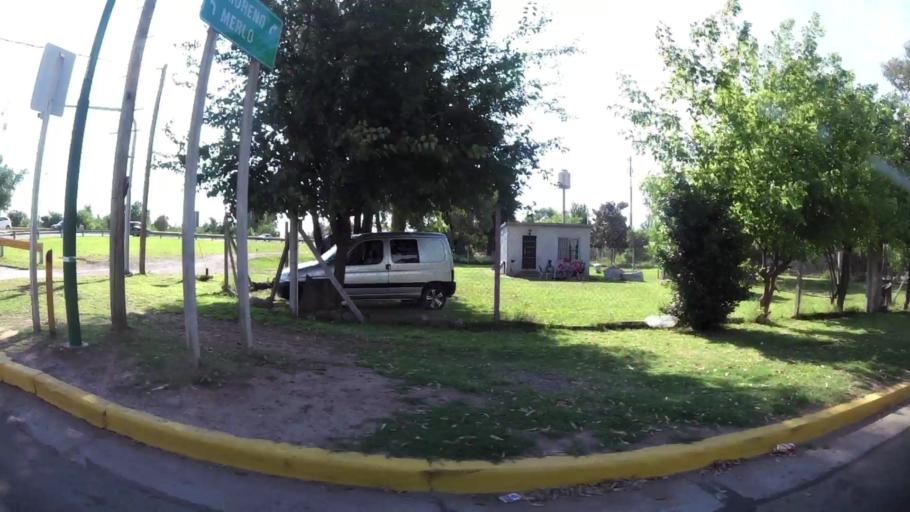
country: AR
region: Buenos Aires
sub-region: Partido de Merlo
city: Merlo
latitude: -34.6598
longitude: -58.7540
